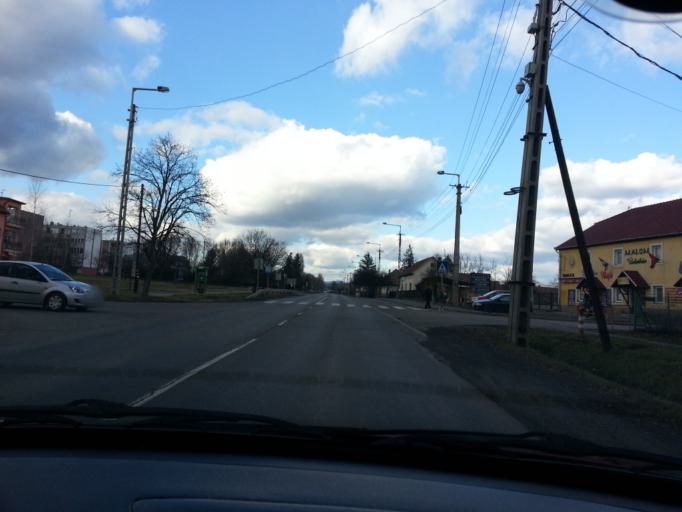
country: HU
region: Nograd
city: Batonyterenye
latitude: 48.0078
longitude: 19.8243
